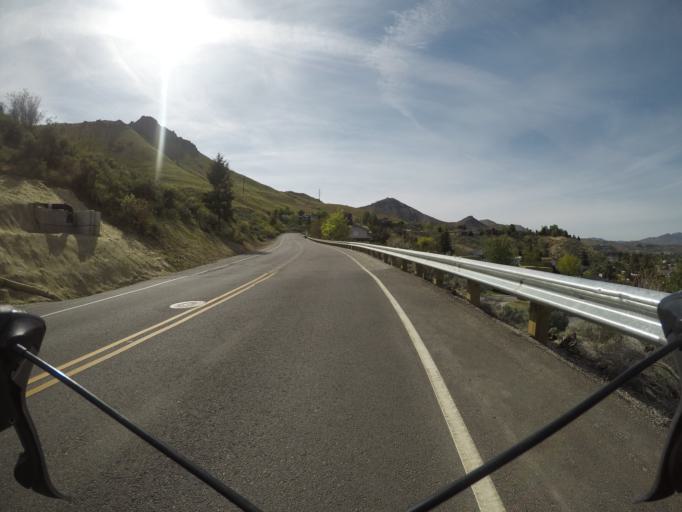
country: US
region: Washington
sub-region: Chelan County
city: Wenatchee
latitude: 47.4091
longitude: -120.3379
